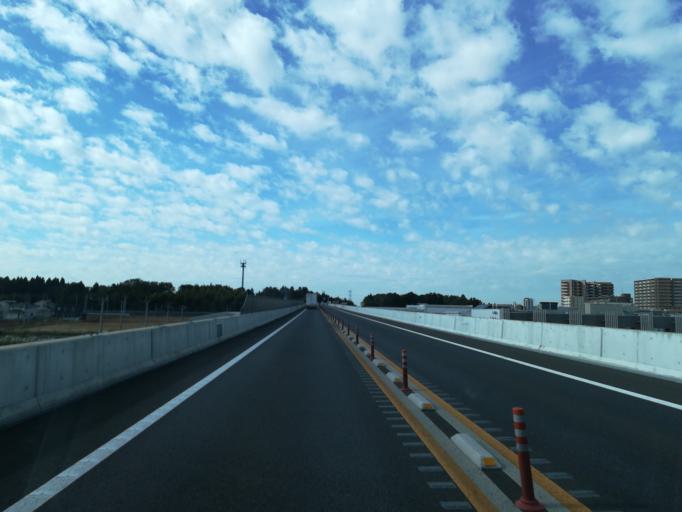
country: JP
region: Ibaraki
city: Mitsukaido
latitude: 36.0559
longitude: 140.0636
